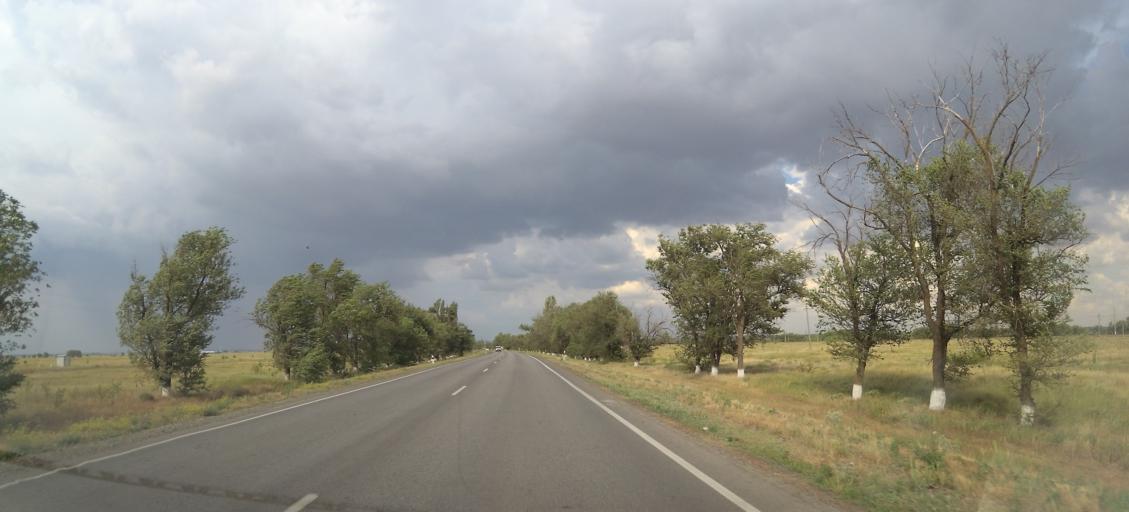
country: RU
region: Rostov
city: Zimovniki
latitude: 47.1308
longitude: 42.4174
